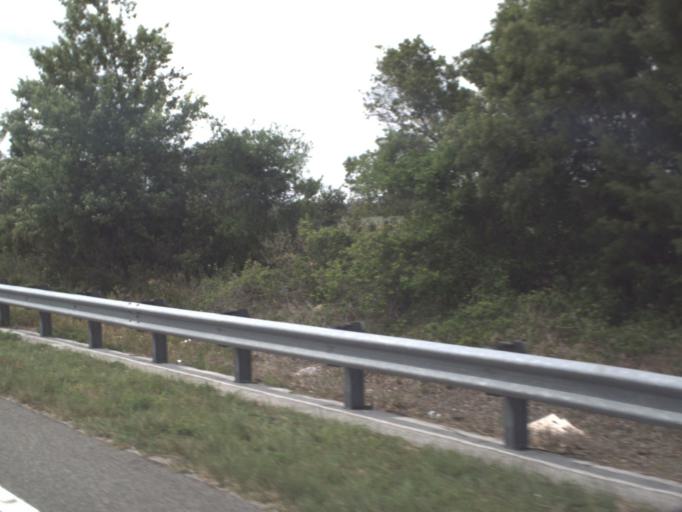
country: US
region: Florida
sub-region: Flagler County
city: Bunnell
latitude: 29.4822
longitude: -81.3589
